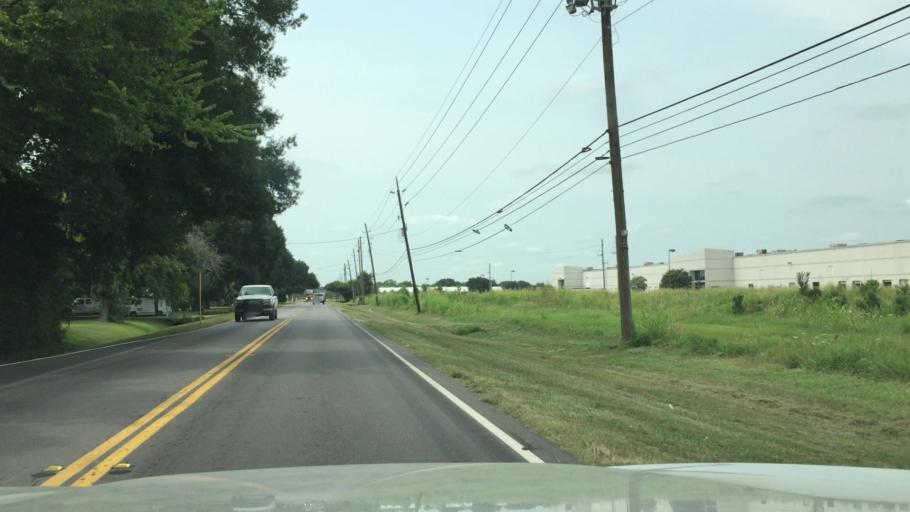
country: US
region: Texas
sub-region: Harris County
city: Jersey Village
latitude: 29.9249
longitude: -95.5480
